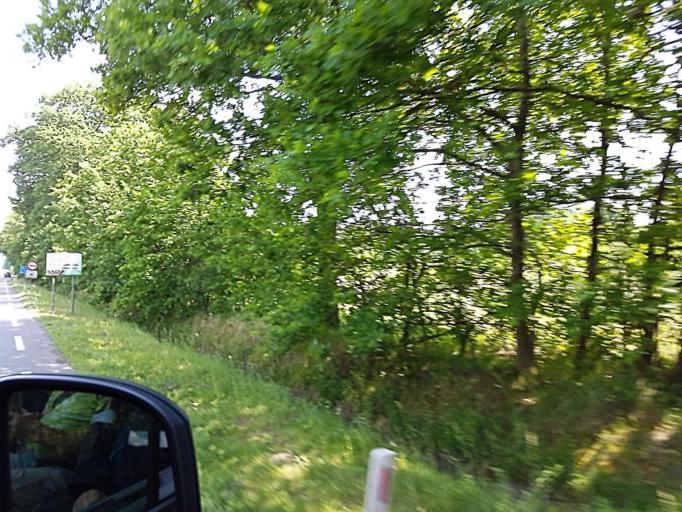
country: BE
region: Flanders
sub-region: Provincie Limburg
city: Overpelt
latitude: 51.2683
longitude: 5.3971
